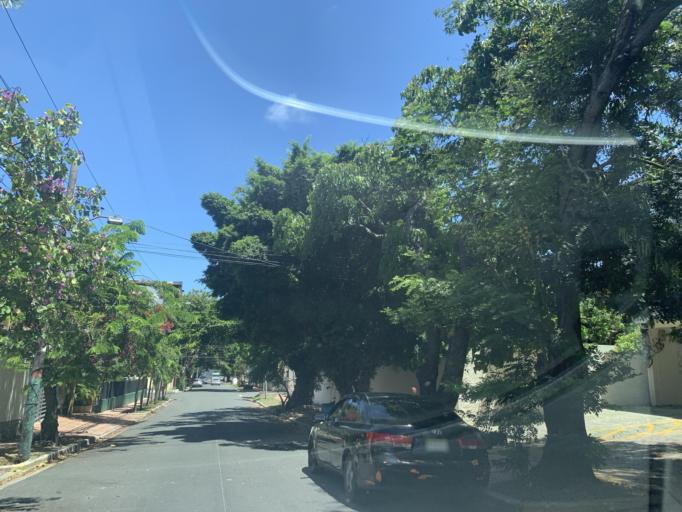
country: DO
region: Nacional
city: Ciudad Nueva
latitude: 18.4699
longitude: -69.9080
